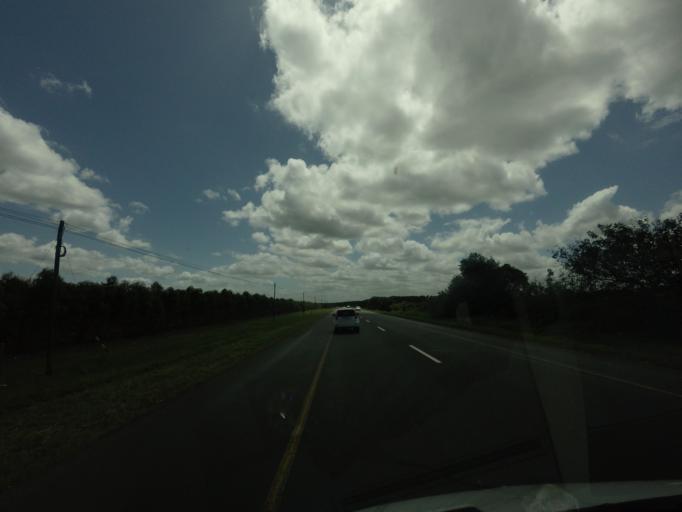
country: ZA
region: KwaZulu-Natal
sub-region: uThungulu District Municipality
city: KwaMbonambi
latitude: -28.5731
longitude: 32.1083
